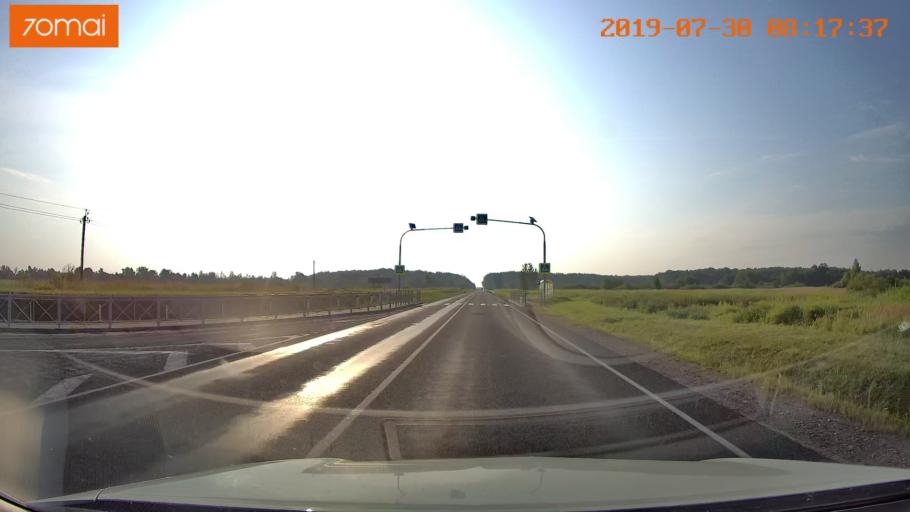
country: RU
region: Kaliningrad
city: Zheleznodorozhnyy
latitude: 54.6357
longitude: 21.4423
